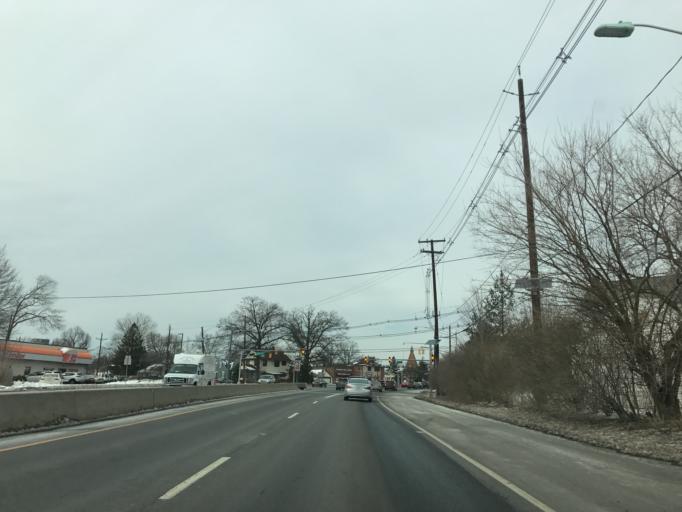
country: US
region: New Jersey
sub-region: Somerset County
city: Raritan
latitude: 40.5724
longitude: -74.6269
